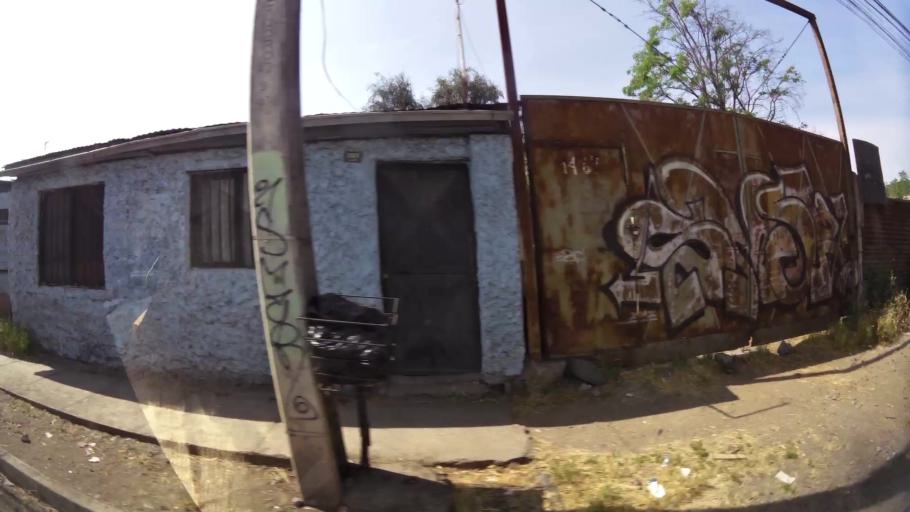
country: CL
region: Santiago Metropolitan
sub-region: Provincia de Santiago
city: Lo Prado
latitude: -33.4283
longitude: -70.7219
